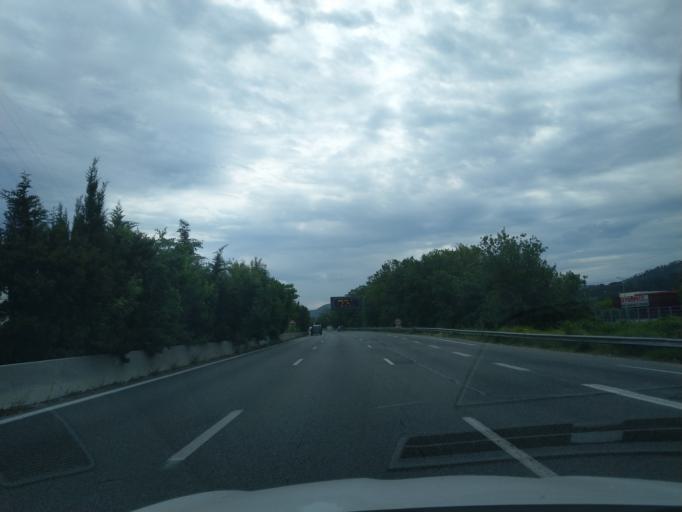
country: FR
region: Provence-Alpes-Cote d'Azur
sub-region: Departement des Bouches-du-Rhone
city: La Penne-sur-Huveaune
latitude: 43.2845
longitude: 5.5177
